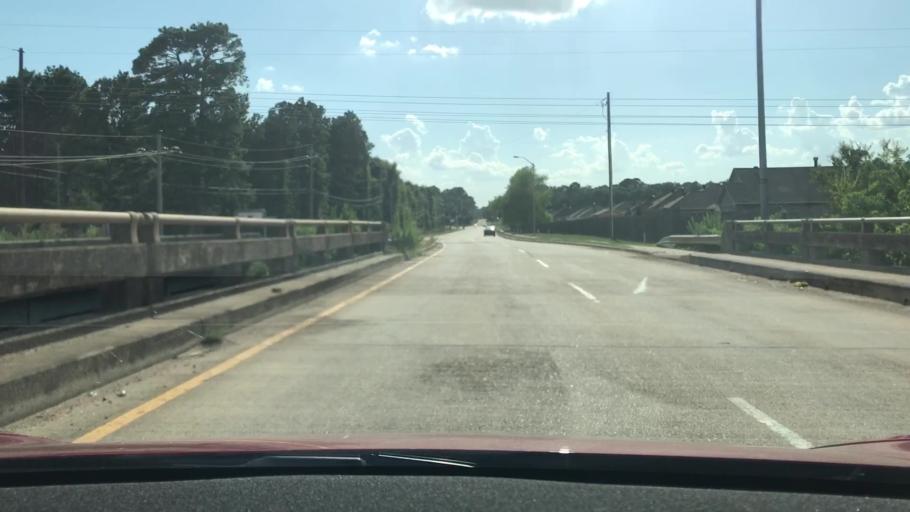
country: US
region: Louisiana
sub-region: Bossier Parish
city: Bossier City
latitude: 32.4130
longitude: -93.7743
